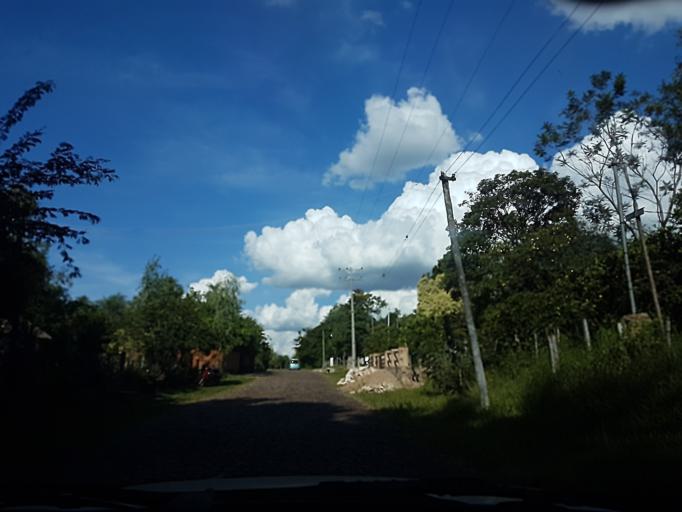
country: PY
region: Cordillera
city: Arroyos y Esteros
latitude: -24.9973
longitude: -57.1412
